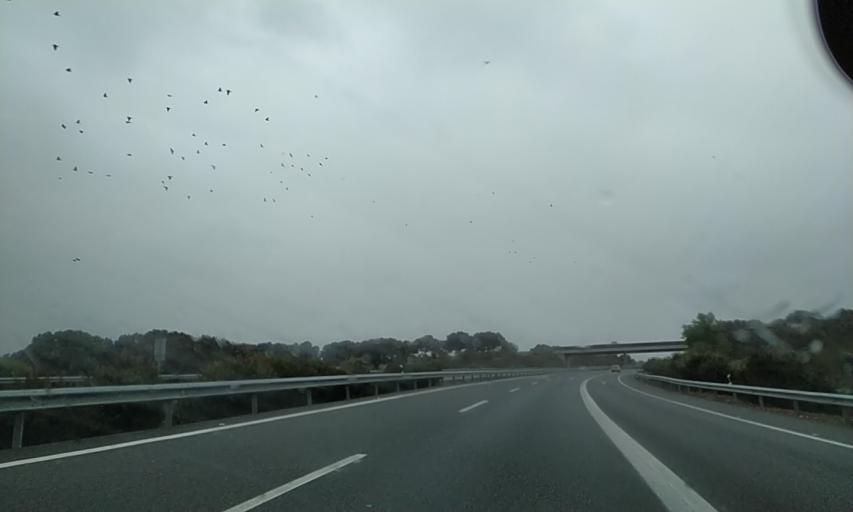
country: ES
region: Extremadura
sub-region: Provincia de Caceres
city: Plasencia
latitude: 40.0320
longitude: -6.1210
